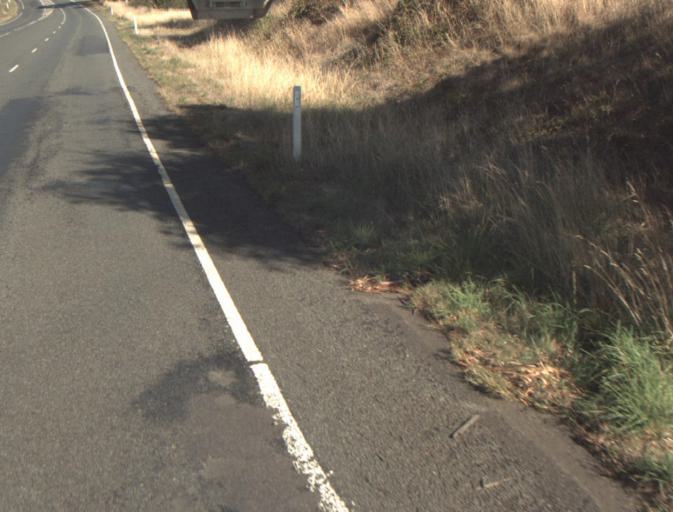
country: AU
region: Tasmania
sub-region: Launceston
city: Mayfield
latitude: -41.3468
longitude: 147.0954
